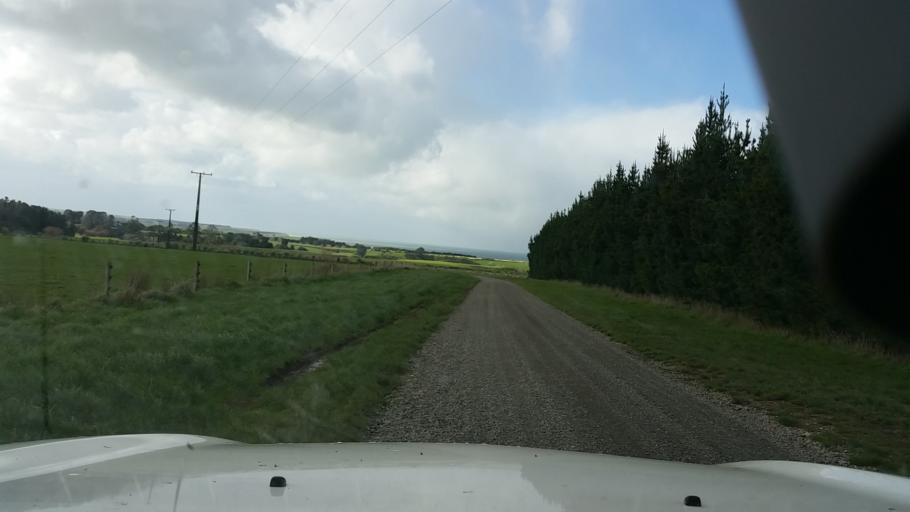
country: NZ
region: Wellington
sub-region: Masterton District
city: Castlepoint
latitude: -41.1834
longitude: 175.9697
